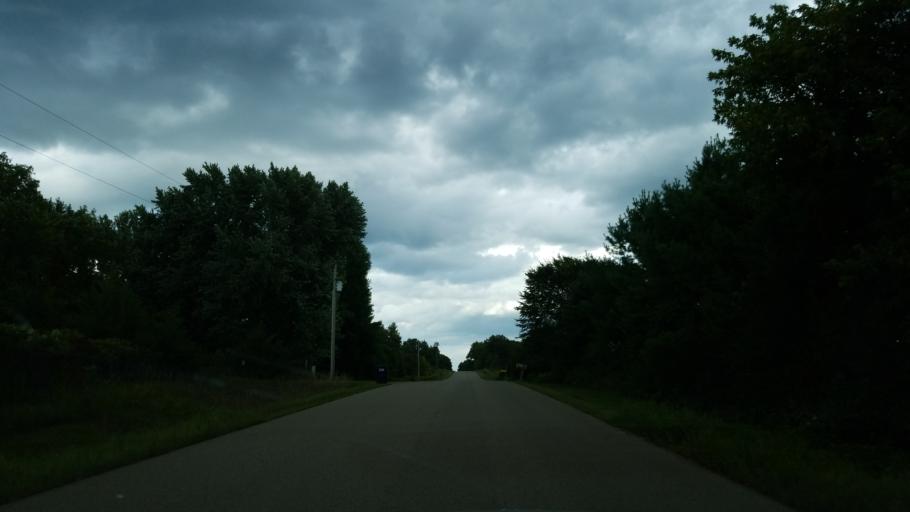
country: US
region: Minnesota
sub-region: Washington County
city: Afton
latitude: 44.8802
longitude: -92.7467
